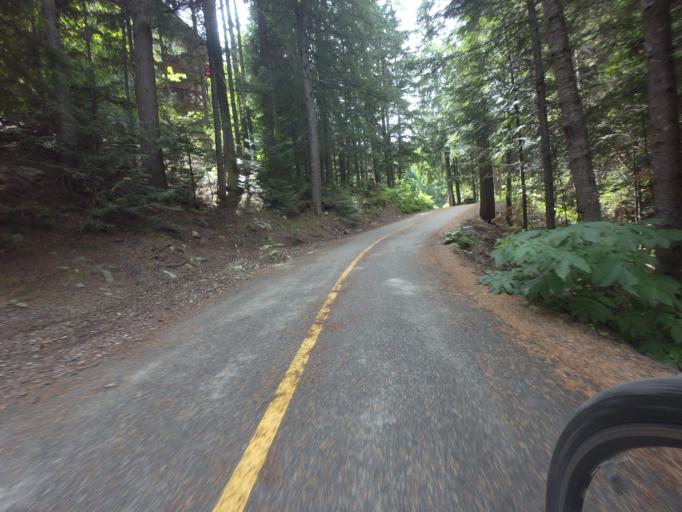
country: CA
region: British Columbia
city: Whistler
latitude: 50.1051
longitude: -122.9843
